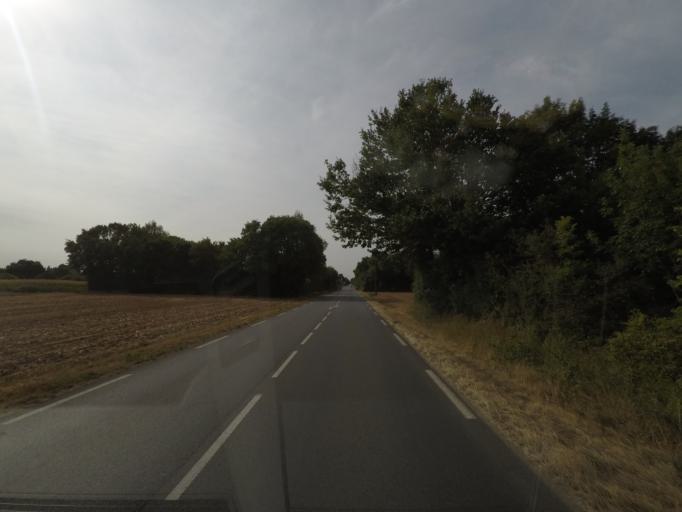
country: FR
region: Poitou-Charentes
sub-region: Departement des Deux-Sevres
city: Lezay
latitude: 46.1753
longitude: -0.0093
